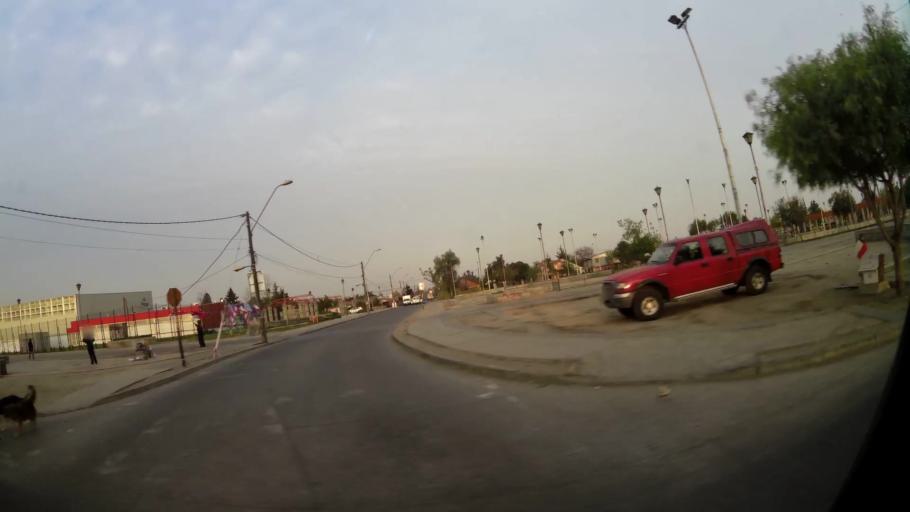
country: CL
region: Santiago Metropolitan
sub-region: Provincia de Santiago
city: Lo Prado
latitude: -33.5156
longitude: -70.7791
